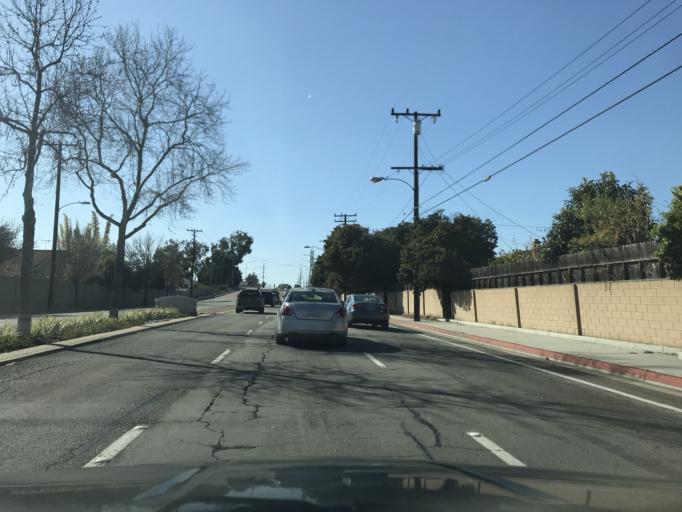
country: US
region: California
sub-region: Orange County
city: Fountain Valley
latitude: 33.6726
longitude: -117.9419
